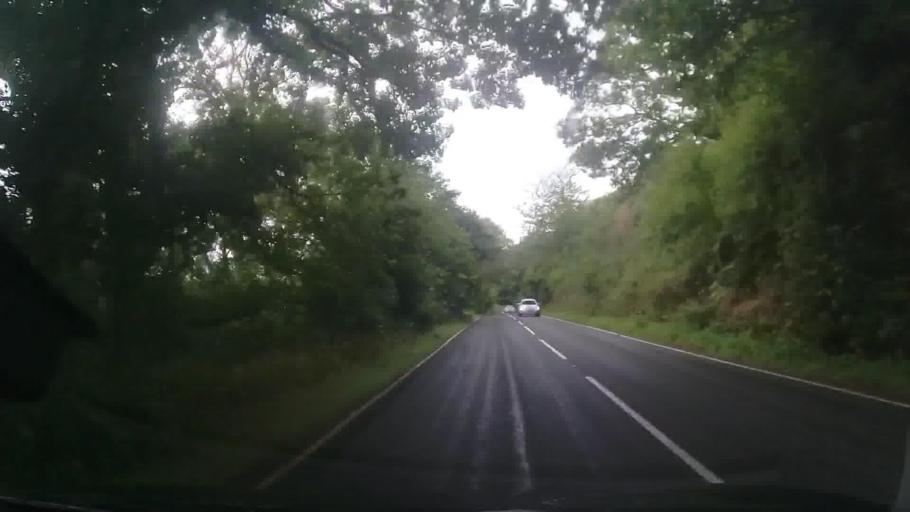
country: GB
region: Wales
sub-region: Gwynedd
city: Barmouth
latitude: 52.7380
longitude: -4.0136
